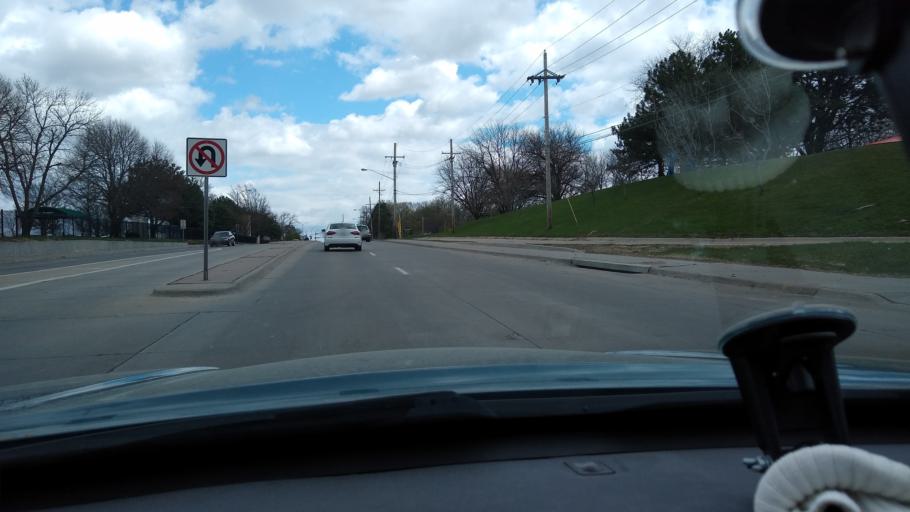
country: US
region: Nebraska
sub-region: Douglas County
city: Ralston
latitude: 41.2342
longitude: -96.0335
